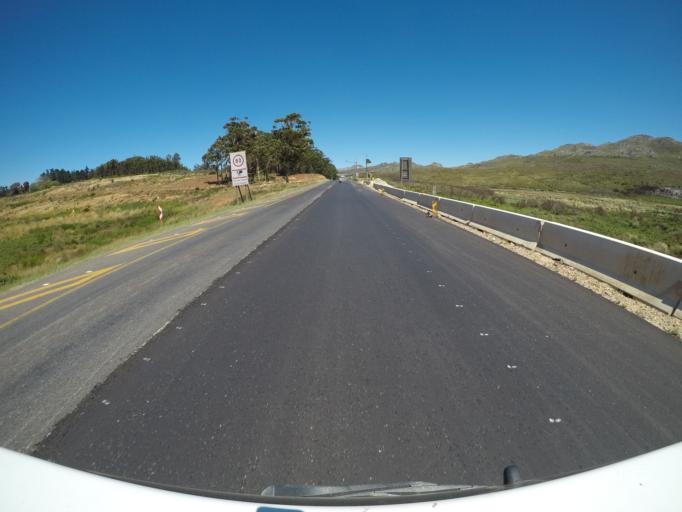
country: ZA
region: Western Cape
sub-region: Overberg District Municipality
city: Grabouw
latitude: -34.1521
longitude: 18.9485
